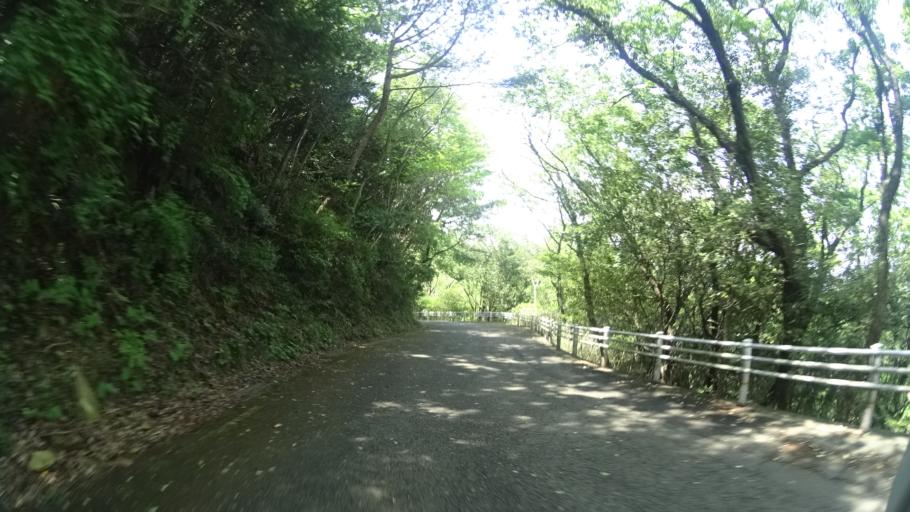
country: JP
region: Tokushima
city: Tokushima-shi
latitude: 34.0677
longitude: 134.5263
